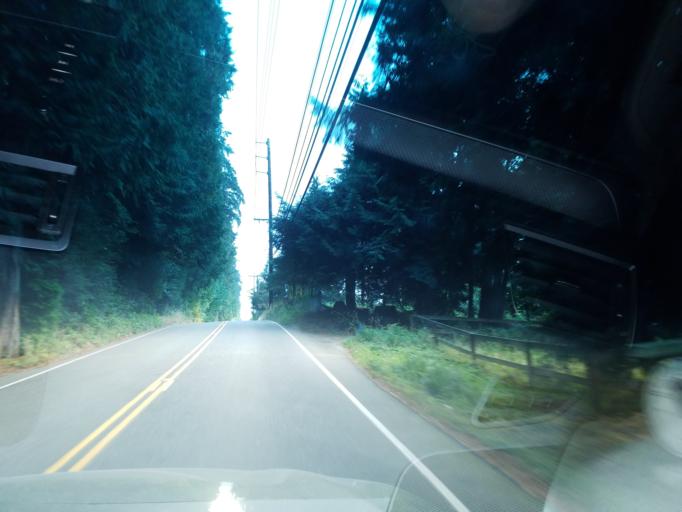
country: US
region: Washington
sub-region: King County
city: Sammamish
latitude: 47.6640
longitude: -122.0629
